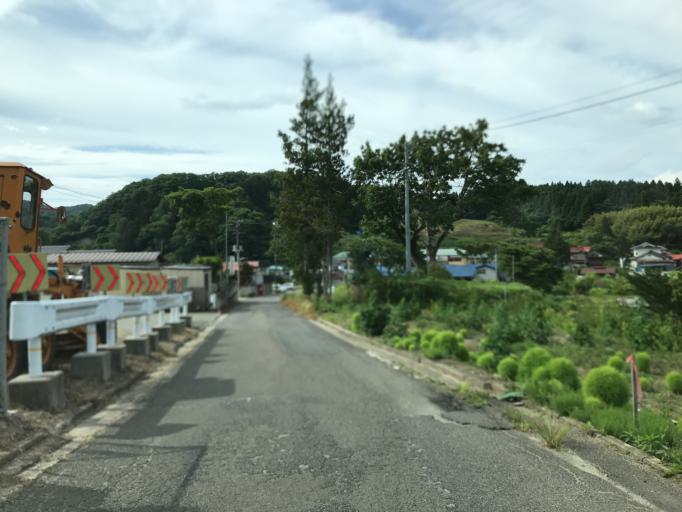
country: JP
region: Fukushima
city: Funehikimachi-funehiki
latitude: 37.5122
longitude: 140.6496
